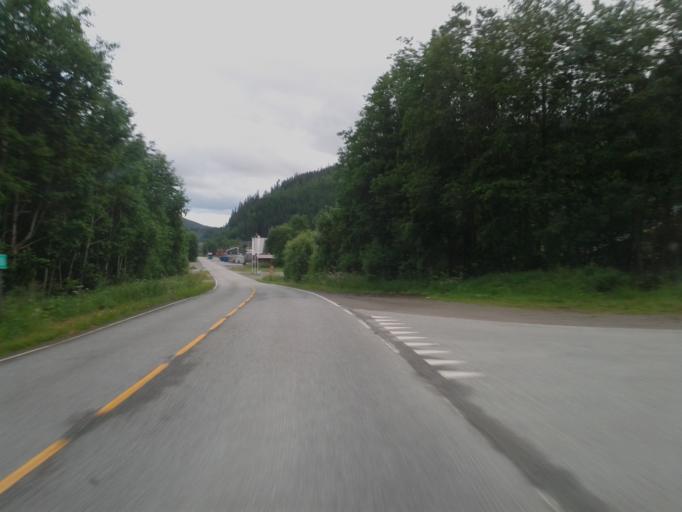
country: NO
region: Sor-Trondelag
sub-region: Midtre Gauldal
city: Storen
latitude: 63.0582
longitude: 10.2867
